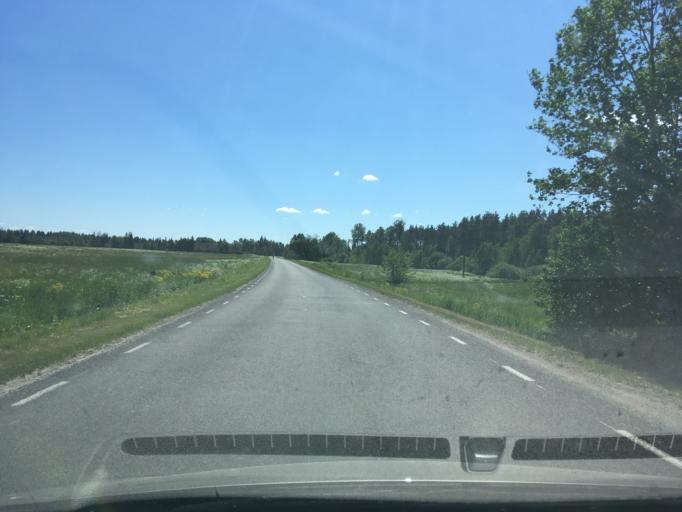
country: EE
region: Raplamaa
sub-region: Kohila vald
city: Kohila
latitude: 59.1739
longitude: 24.8451
